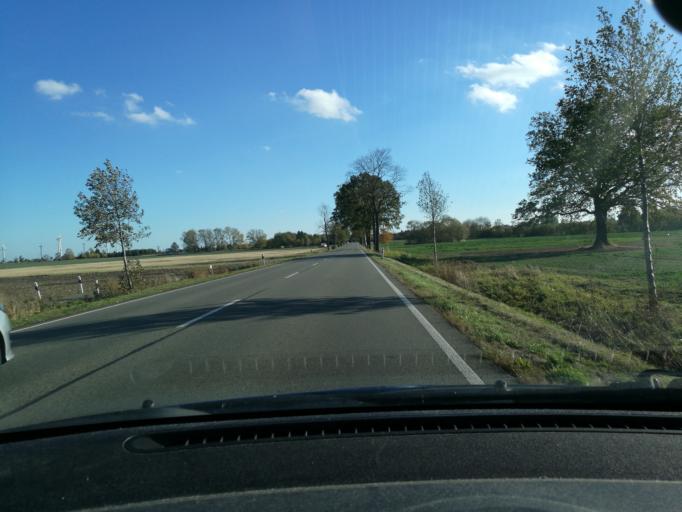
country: DE
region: Brandenburg
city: Karstadt
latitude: 53.1409
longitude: 11.7728
